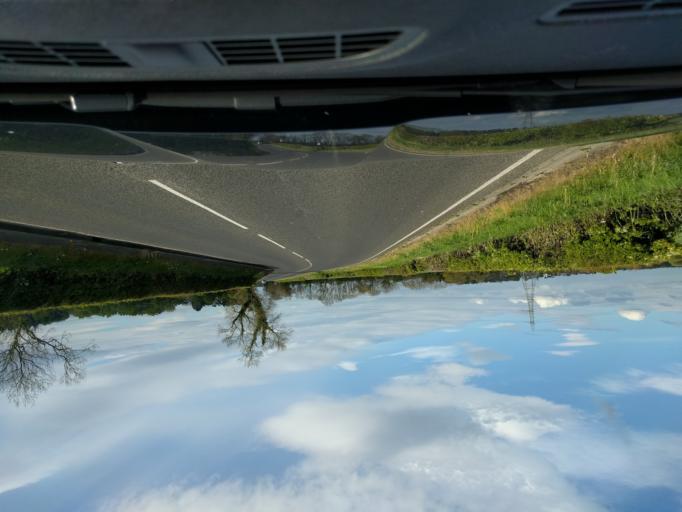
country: GB
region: England
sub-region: Northumberland
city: Stannington
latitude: 55.1400
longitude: -1.6514
